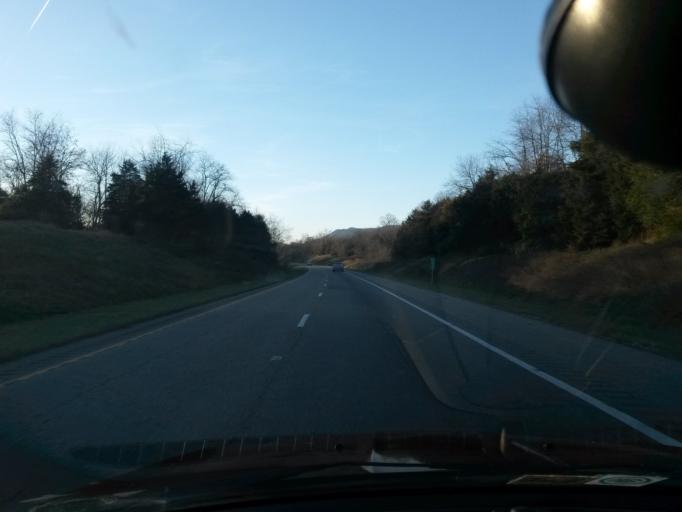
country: US
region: Virginia
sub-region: Rockbridge County
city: East Lexington
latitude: 37.8433
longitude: -79.4535
